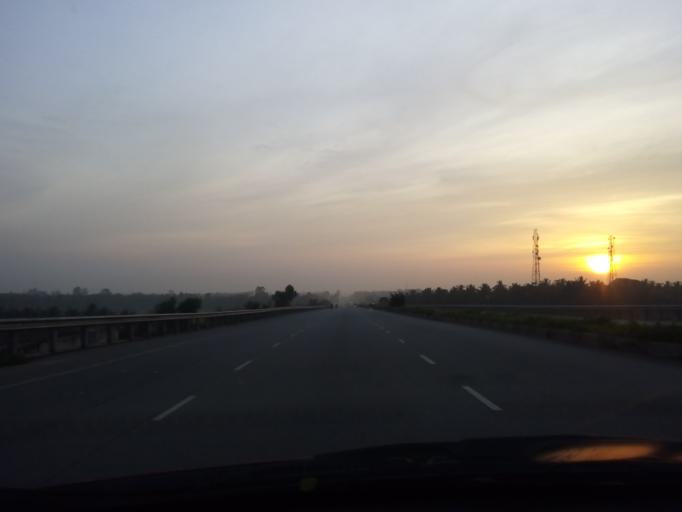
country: IN
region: Karnataka
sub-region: Bangalore Rural
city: Devanhalli
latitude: 13.2161
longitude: 77.6772
